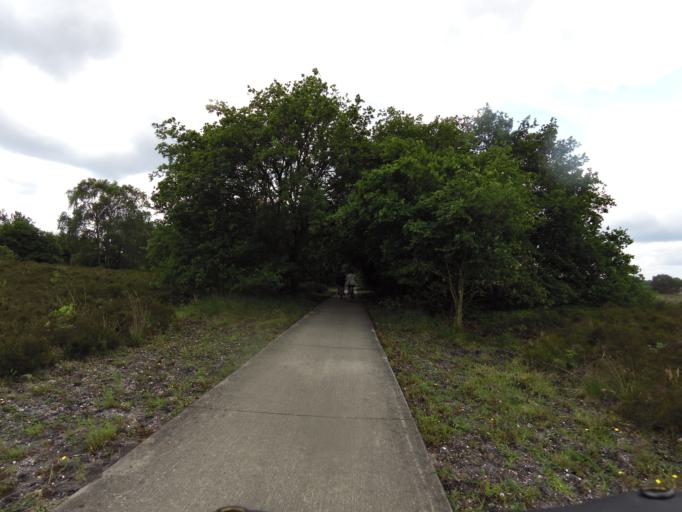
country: NL
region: Gelderland
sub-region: Gemeente Apeldoorn
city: Uddel
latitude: 52.3129
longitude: 5.8126
